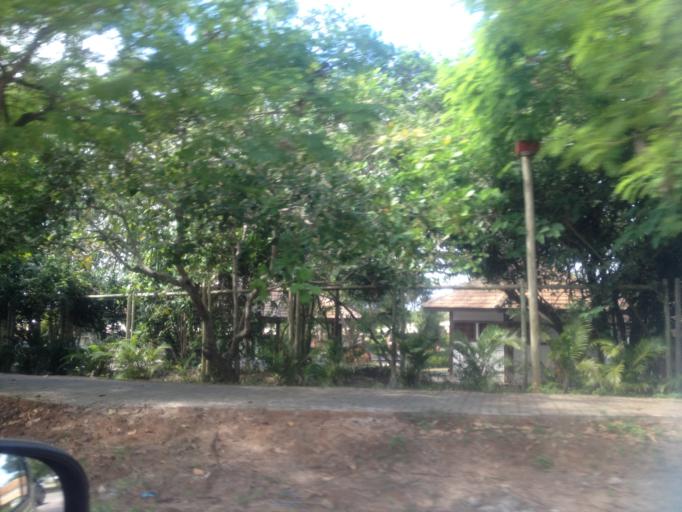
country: BR
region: Bahia
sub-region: Mata De Sao Joao
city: Mata de Sao Joao
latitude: -12.5762
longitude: -38.0168
